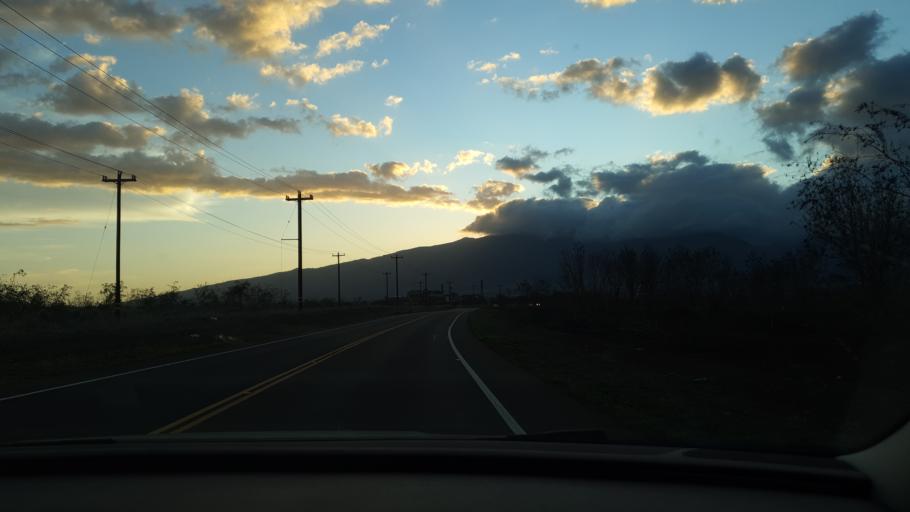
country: US
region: Hawaii
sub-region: Maui County
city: Kahului
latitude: 20.8718
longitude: -156.4415
